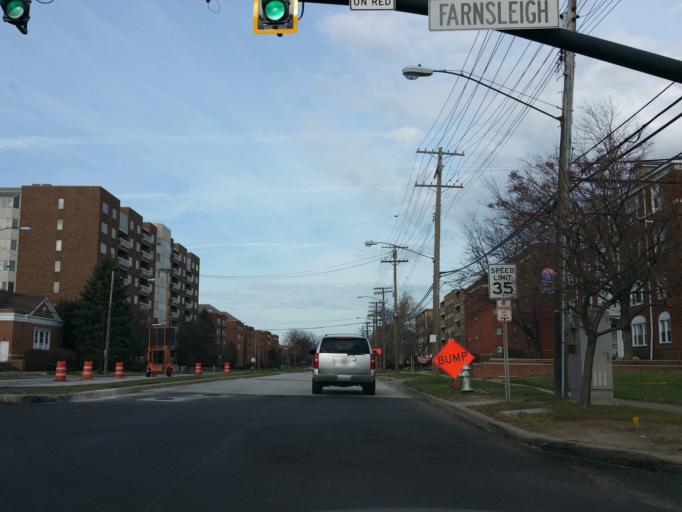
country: US
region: Ohio
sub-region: Cuyahoga County
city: Shaker Heights
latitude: 41.4676
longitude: -81.5362
